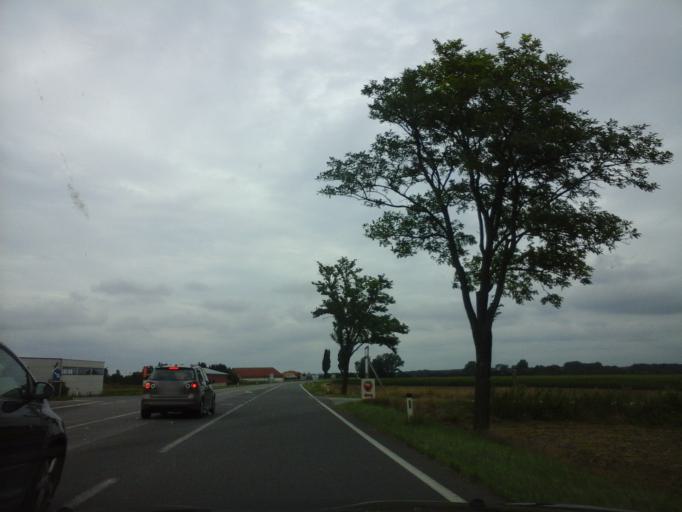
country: AT
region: Lower Austria
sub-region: Politischer Bezirk Ganserndorf
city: Engelhartstetten
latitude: 48.1786
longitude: 16.8916
